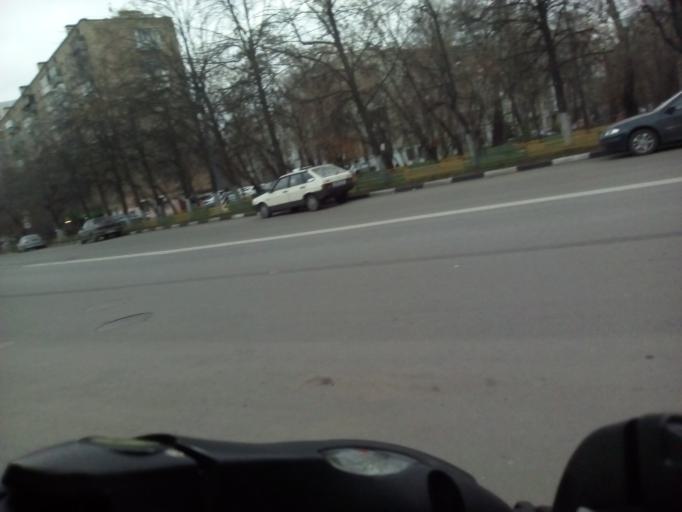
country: RU
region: Moscow
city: Lefortovo
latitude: 55.7636
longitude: 37.7186
